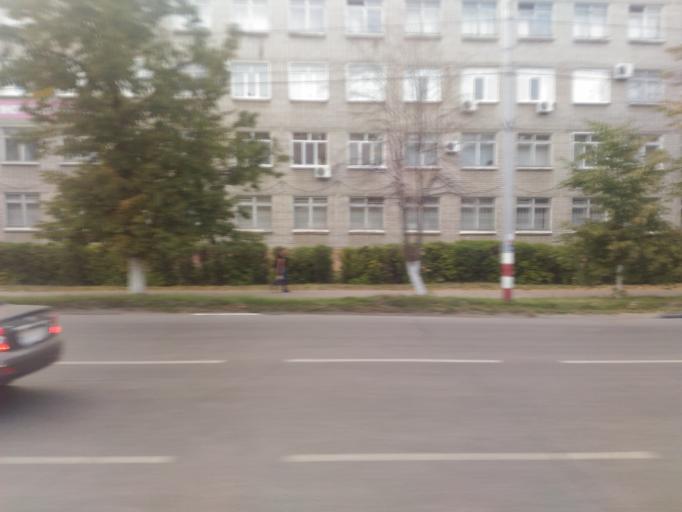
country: RU
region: Ulyanovsk
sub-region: Ulyanovskiy Rayon
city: Ulyanovsk
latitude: 54.2912
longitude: 48.3097
